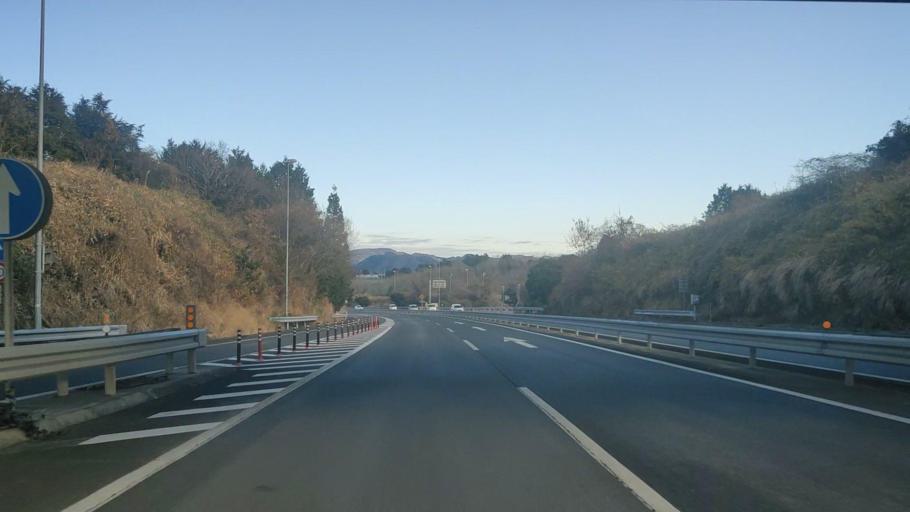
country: JP
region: Oita
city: Hiji
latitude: 33.4233
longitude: 131.4244
